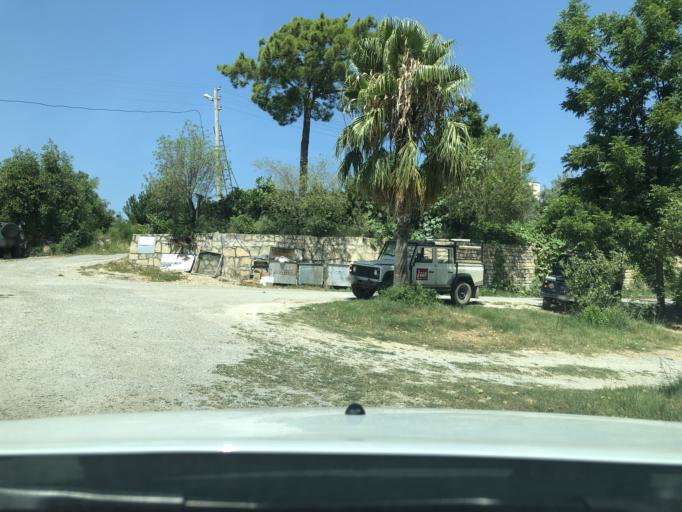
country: TR
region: Antalya
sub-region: Manavgat
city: Kizilagac
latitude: 36.8571
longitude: 31.5525
